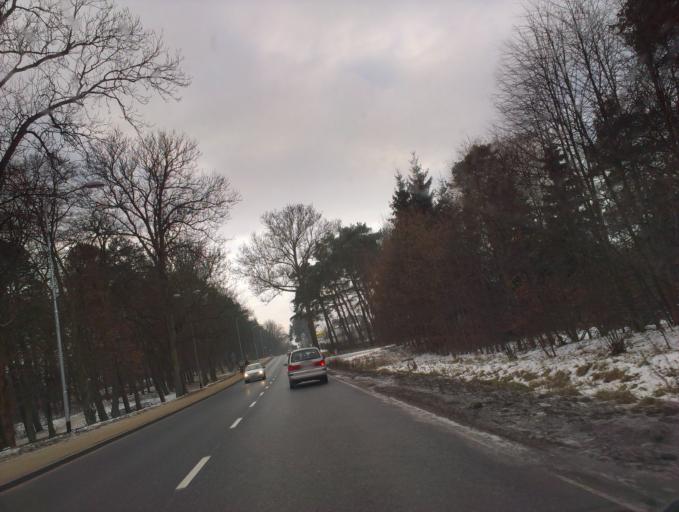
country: PL
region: Greater Poland Voivodeship
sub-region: Powiat zlotowski
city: Jastrowie
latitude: 53.4122
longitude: 16.8004
